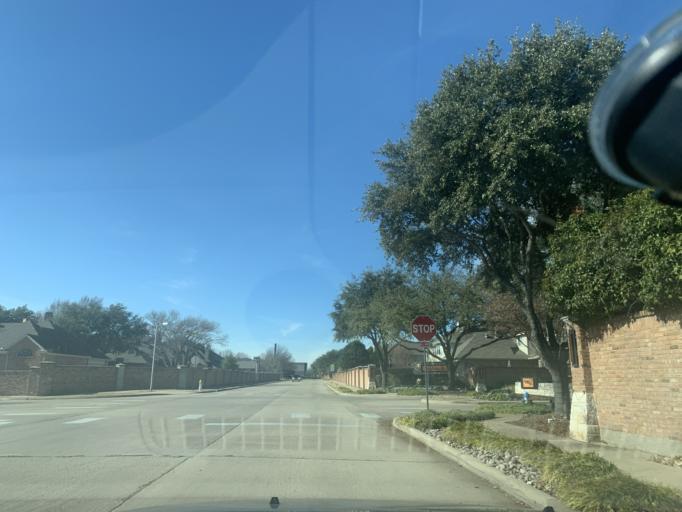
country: US
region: Texas
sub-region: Denton County
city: The Colony
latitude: 33.0499
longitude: -96.8228
